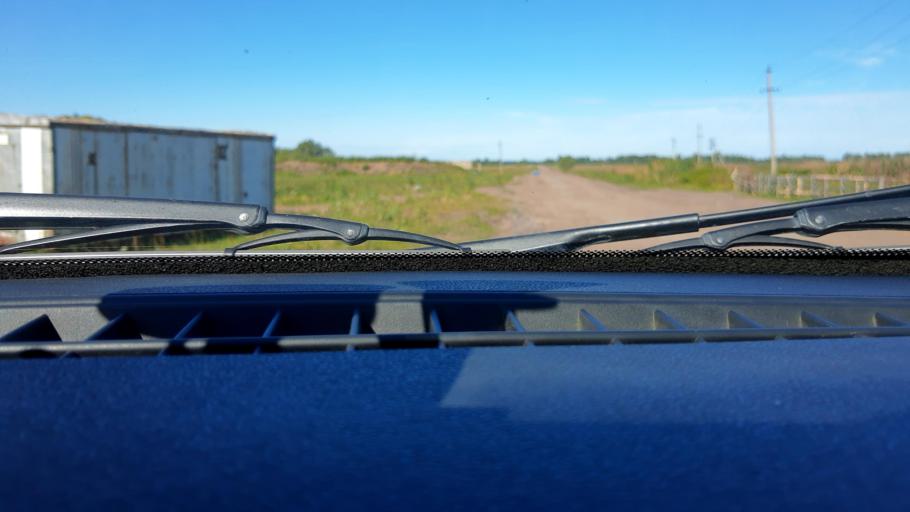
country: RU
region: Bashkortostan
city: Asanovo
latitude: 54.8197
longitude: 55.6231
